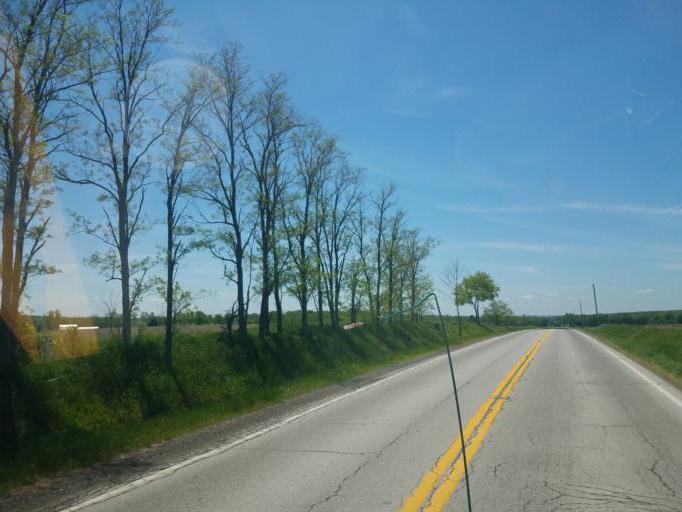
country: US
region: Ohio
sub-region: Ashland County
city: Ashland
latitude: 40.9733
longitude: -82.2426
